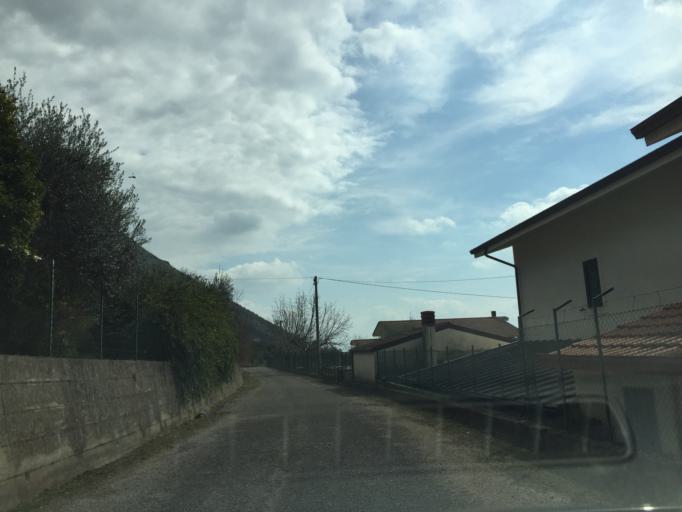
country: IT
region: Latium
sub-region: Provincia di Frosinone
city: Castrocielo
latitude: 41.5288
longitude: 13.6998
